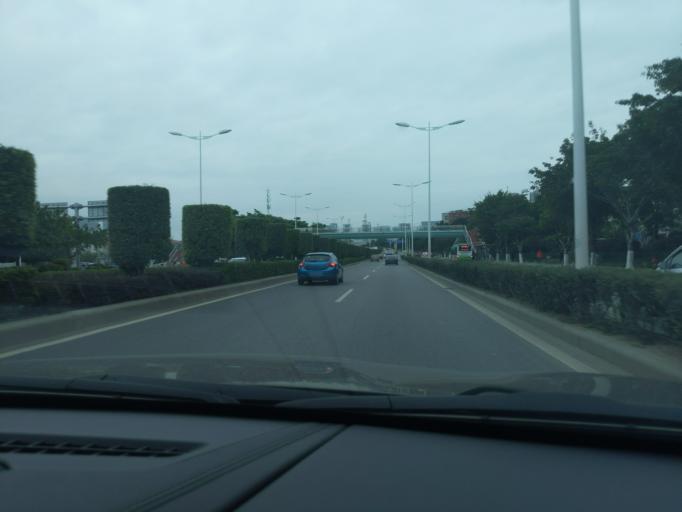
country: CN
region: Fujian
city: Liuwudian
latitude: 24.5327
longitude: 118.1639
